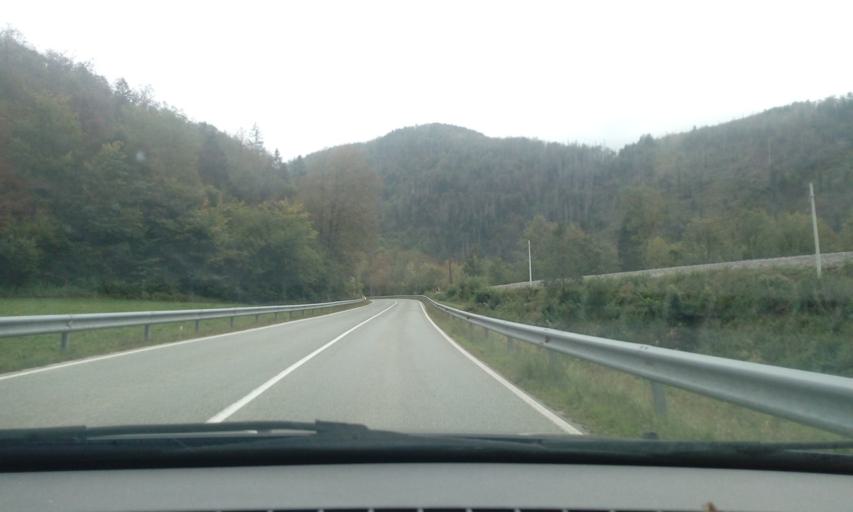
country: SI
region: Bohinj
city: Bohinjska Bistrica
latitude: 46.2827
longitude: 13.9660
